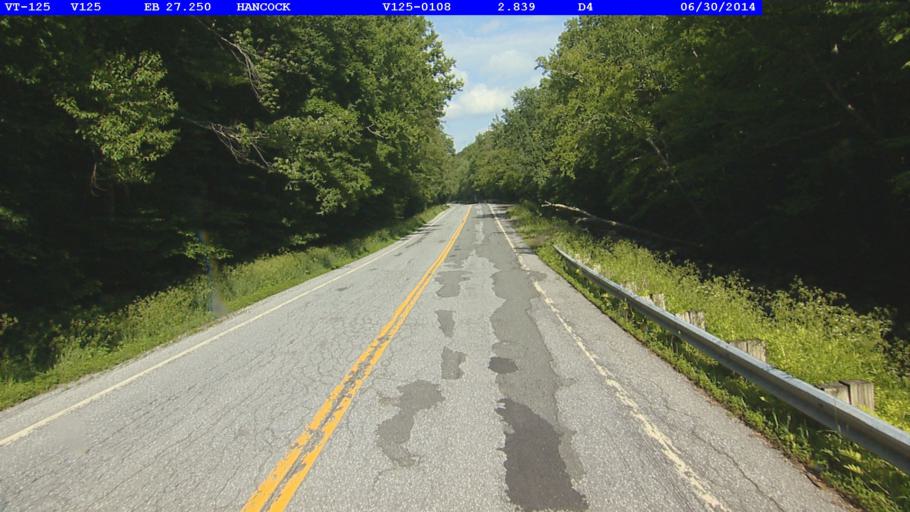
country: US
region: Vermont
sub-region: Rutland County
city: Brandon
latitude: 43.9270
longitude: -72.9256
